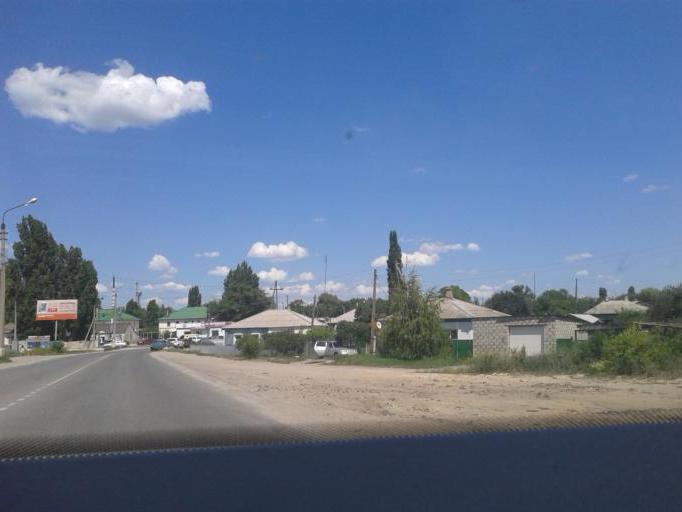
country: RU
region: Volgograd
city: Frolovo
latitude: 49.7579
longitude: 43.6556
